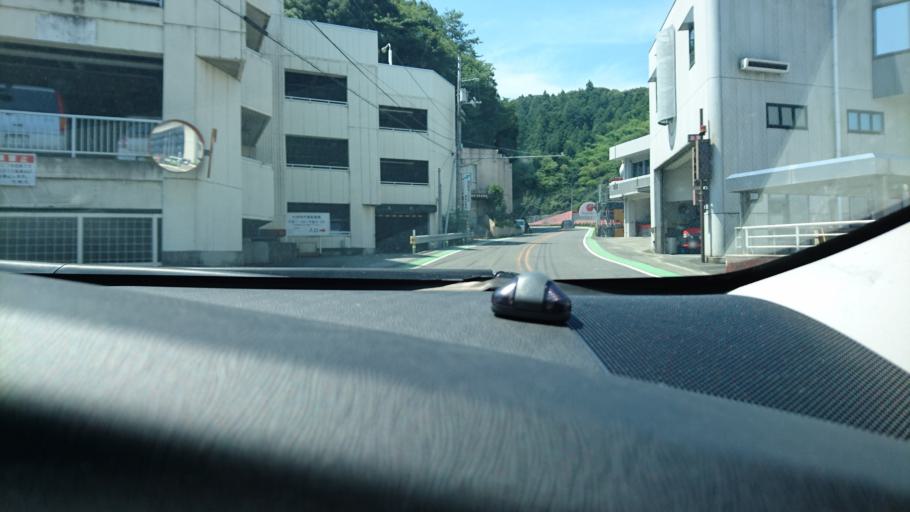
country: JP
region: Ehime
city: Ozu
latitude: 33.5059
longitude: 132.5448
